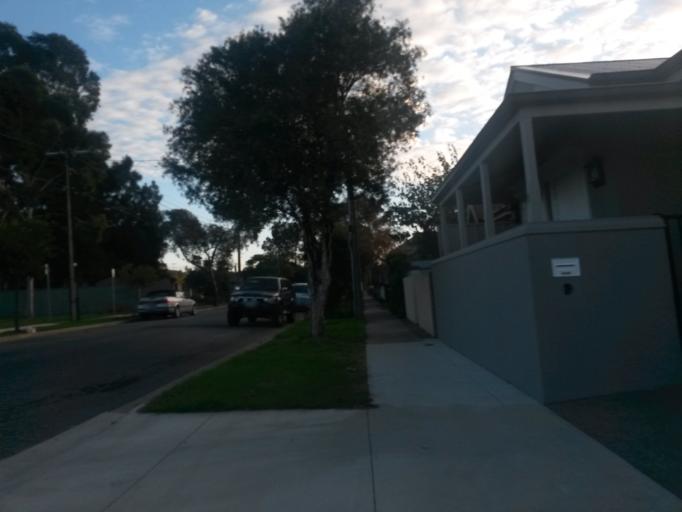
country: AU
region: South Australia
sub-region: Port Adelaide Enfield
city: Birkenhead
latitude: -34.8513
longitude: 138.5060
